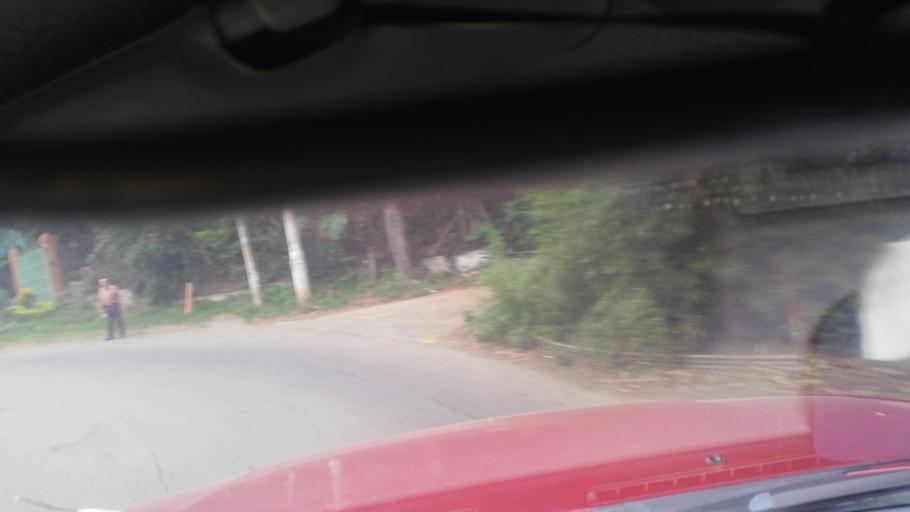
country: CO
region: Valle del Cauca
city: Cali
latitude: 3.4820
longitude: -76.5516
